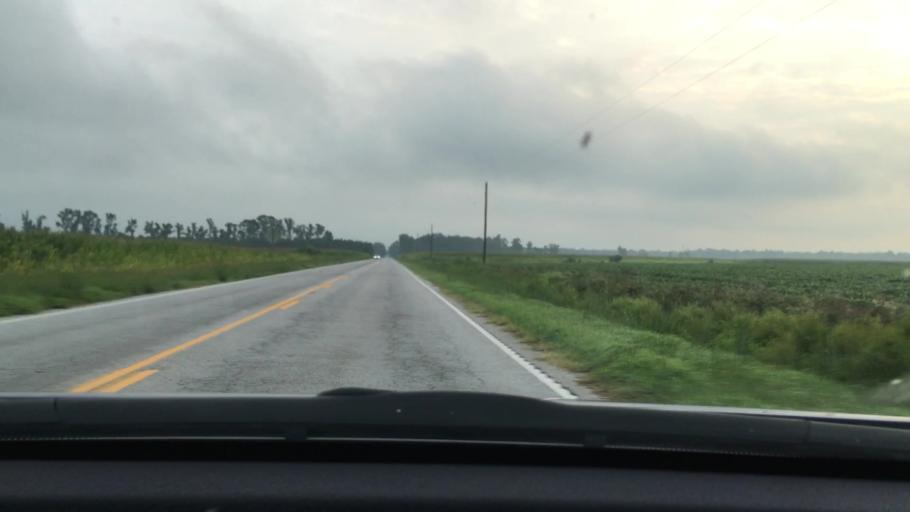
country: US
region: South Carolina
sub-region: Sumter County
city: East Sumter
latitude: 34.0108
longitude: -80.2852
